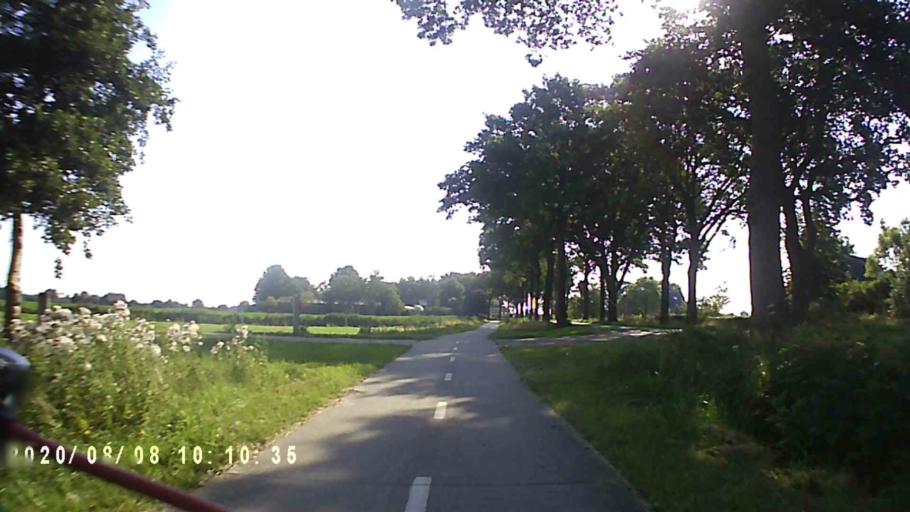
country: NL
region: Groningen
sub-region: Gemeente Leek
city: Leek
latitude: 53.1214
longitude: 6.3726
